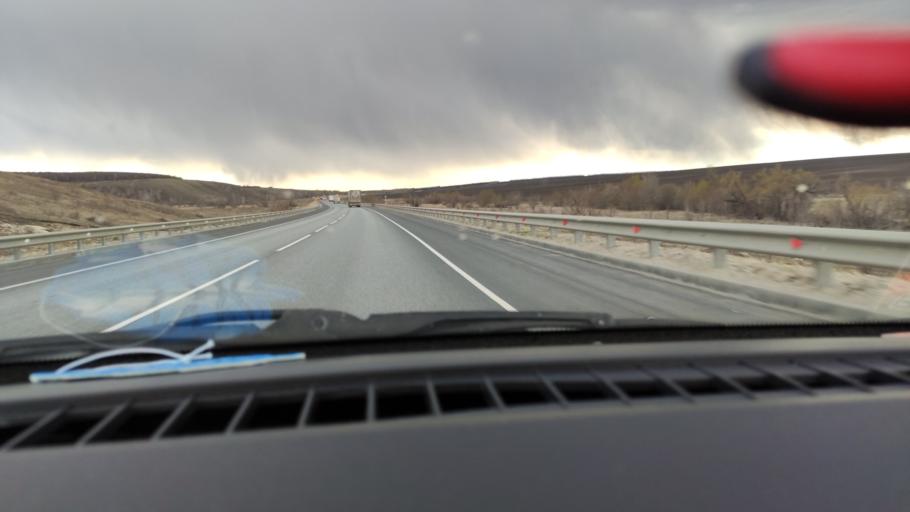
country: RU
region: Saratov
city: Yelshanka
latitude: 51.8677
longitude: 46.5023
